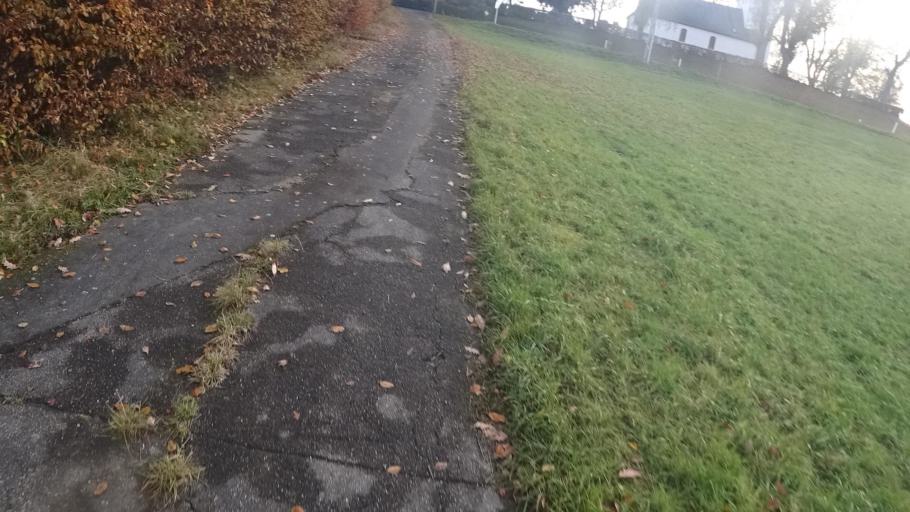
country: DE
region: Rheinland-Pfalz
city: Pfalzfeld
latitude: 50.1154
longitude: 7.5767
